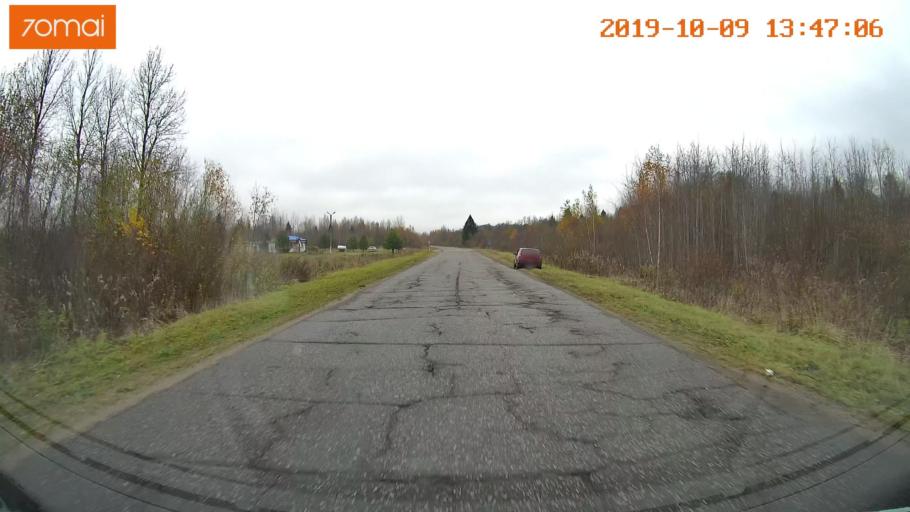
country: RU
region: Kostroma
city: Buy
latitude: 58.3891
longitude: 41.2225
